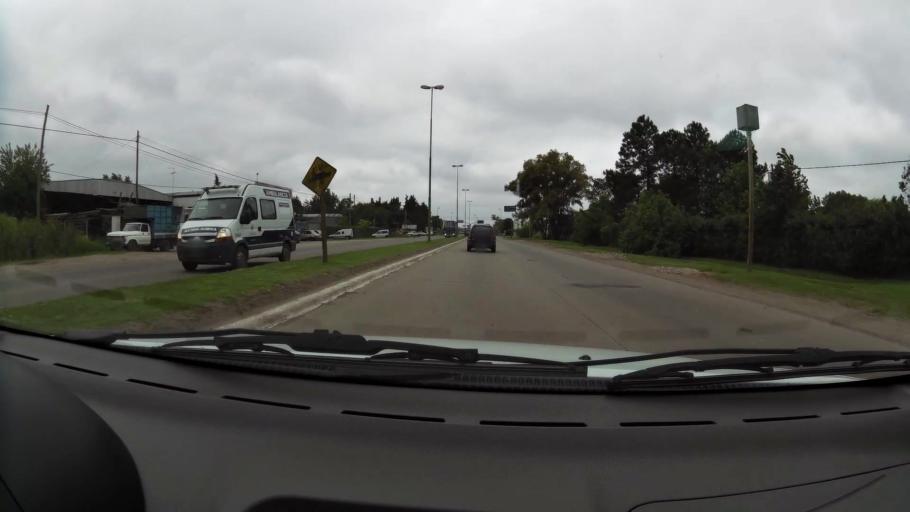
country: AR
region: Buenos Aires
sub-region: Partido de La Plata
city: La Plata
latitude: -35.0074
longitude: -58.0614
